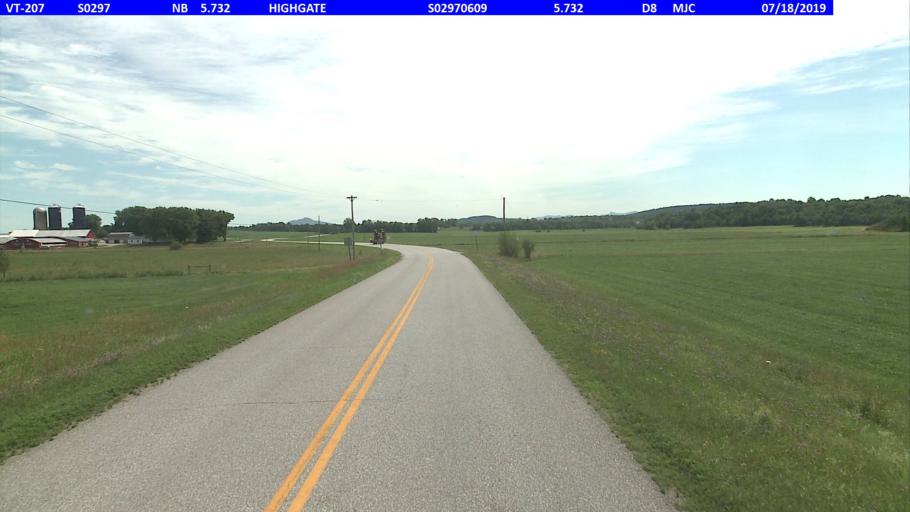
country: CA
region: Quebec
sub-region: Monteregie
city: Bedford
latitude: 45.0067
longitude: -72.9913
